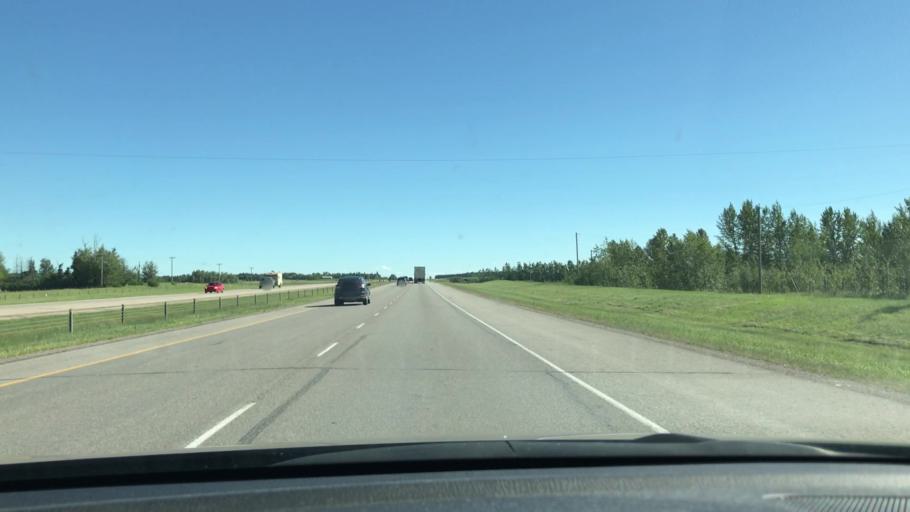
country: CA
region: Alberta
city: Olds
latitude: 51.9055
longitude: -114.0262
